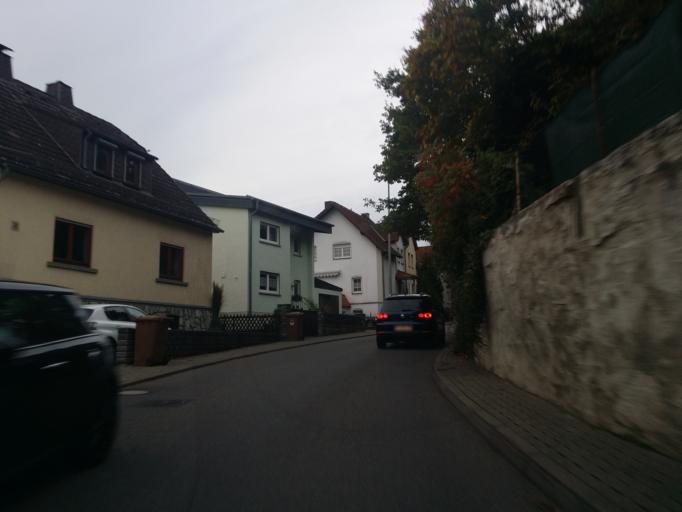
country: DE
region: Hesse
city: Eppstein
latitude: 50.1758
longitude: 8.3685
